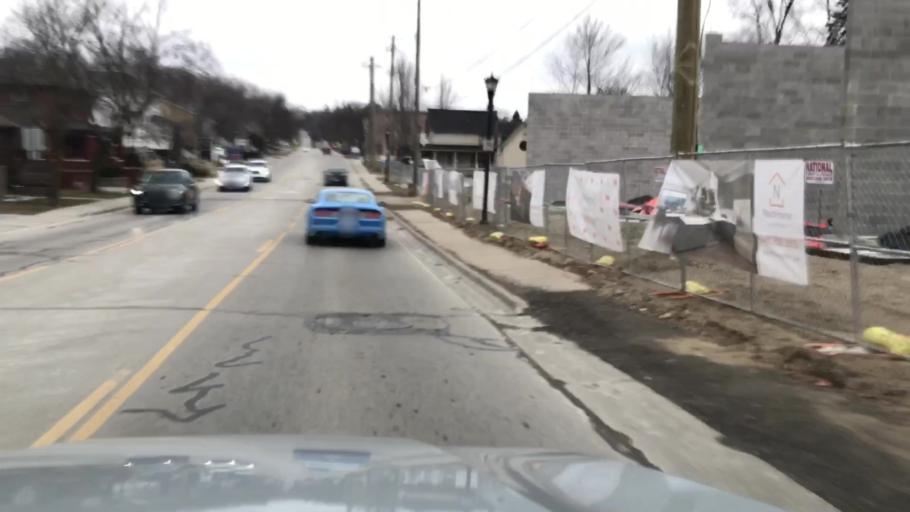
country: US
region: Michigan
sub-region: Wayne County
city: Northville
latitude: 42.4332
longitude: -83.4832
